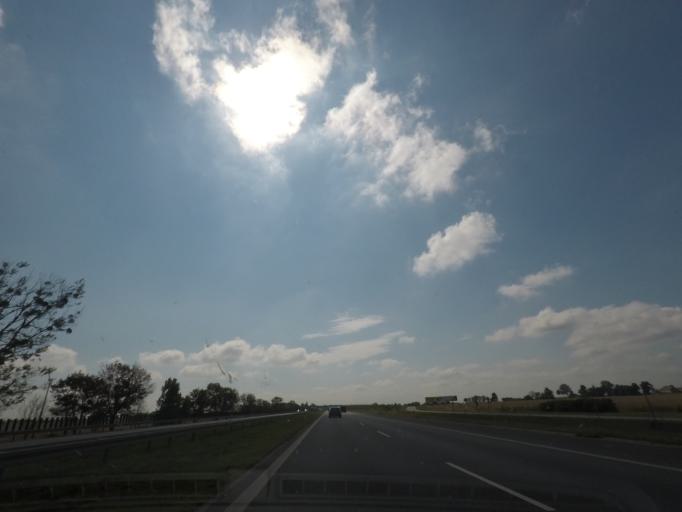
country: PL
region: Kujawsko-Pomorskie
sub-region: Powiat aleksandrowski
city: Ciechocinek
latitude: 52.8506
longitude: 18.7806
